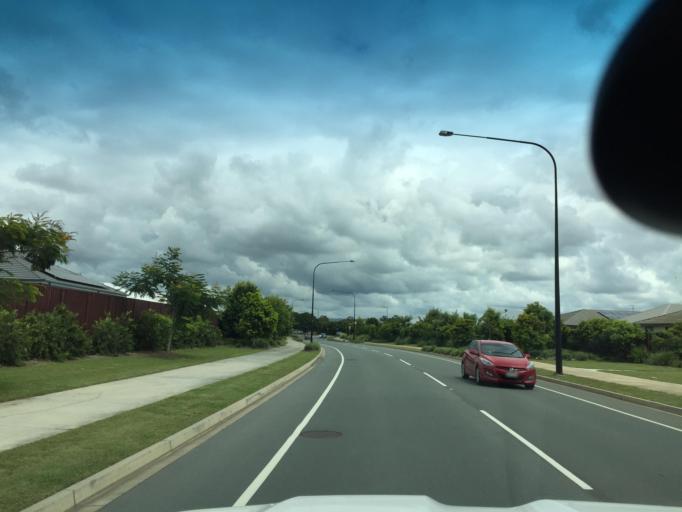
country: AU
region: Queensland
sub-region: Moreton Bay
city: Caboolture South
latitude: -27.0953
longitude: 152.9612
